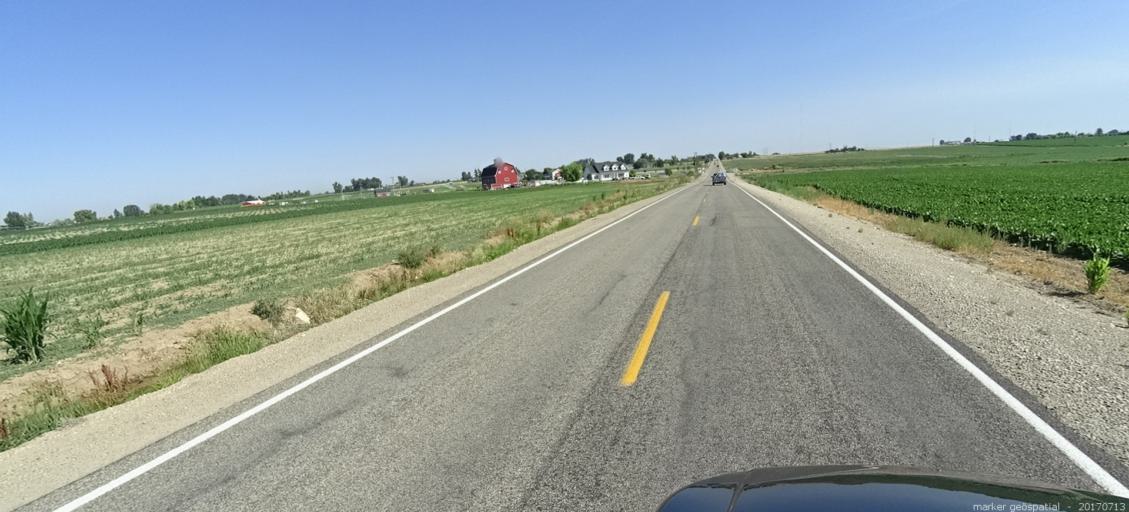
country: US
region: Idaho
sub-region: Ada County
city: Kuna
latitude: 43.5372
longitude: -116.4138
